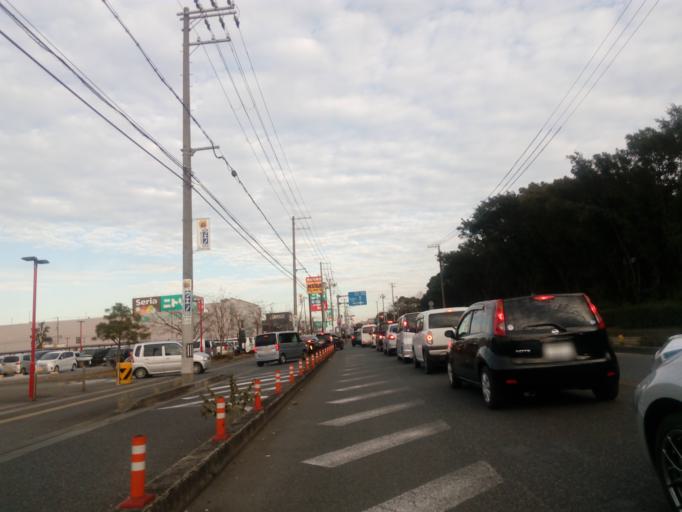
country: JP
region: Hyogo
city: Himeji
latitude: 34.7954
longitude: 134.6367
